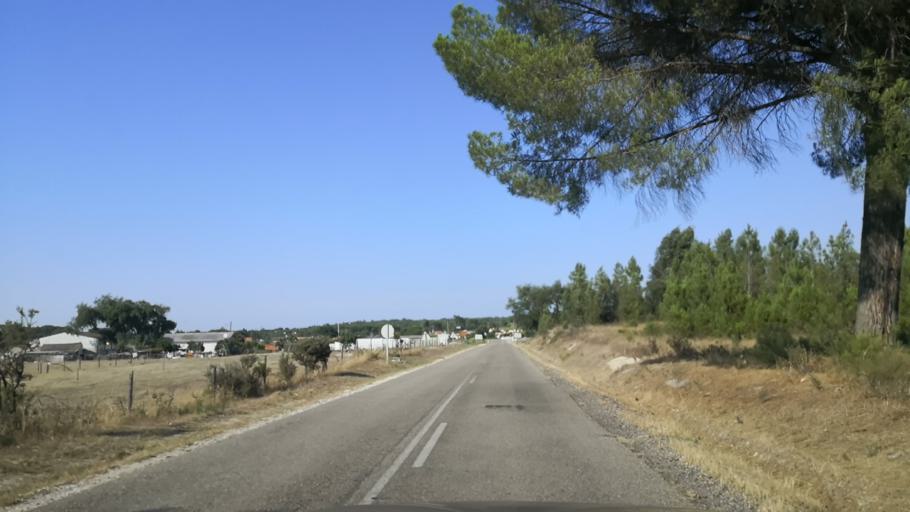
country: PT
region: Santarem
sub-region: Coruche
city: Coruche
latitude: 38.8835
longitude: -8.5385
